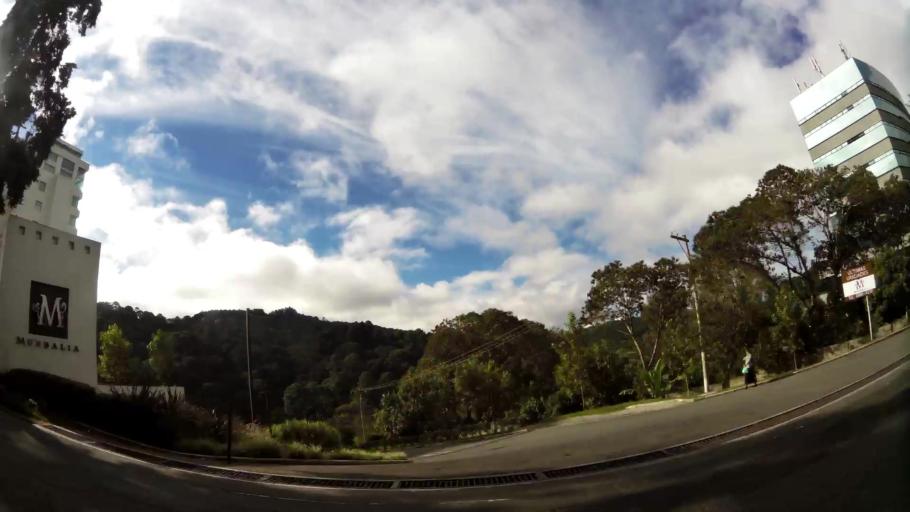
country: GT
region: Guatemala
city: Santa Catarina Pinula
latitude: 14.5614
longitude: -90.4777
